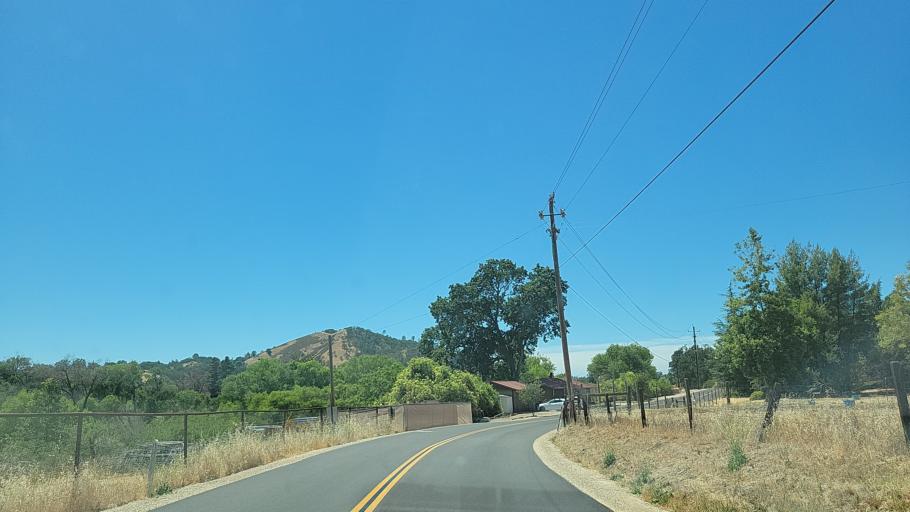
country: US
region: California
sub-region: San Luis Obispo County
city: Atascadero
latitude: 35.4878
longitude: -120.6371
